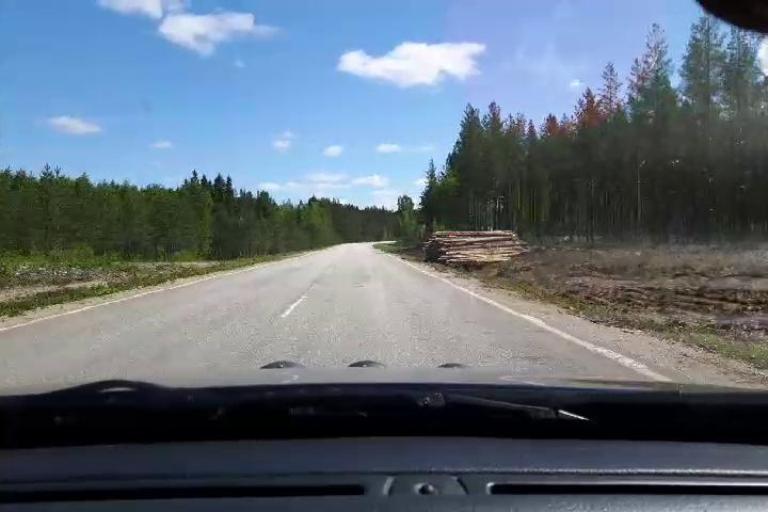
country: SE
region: Vaesternorrland
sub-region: Ange Kommun
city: Ange
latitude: 62.0550
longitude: 15.1348
